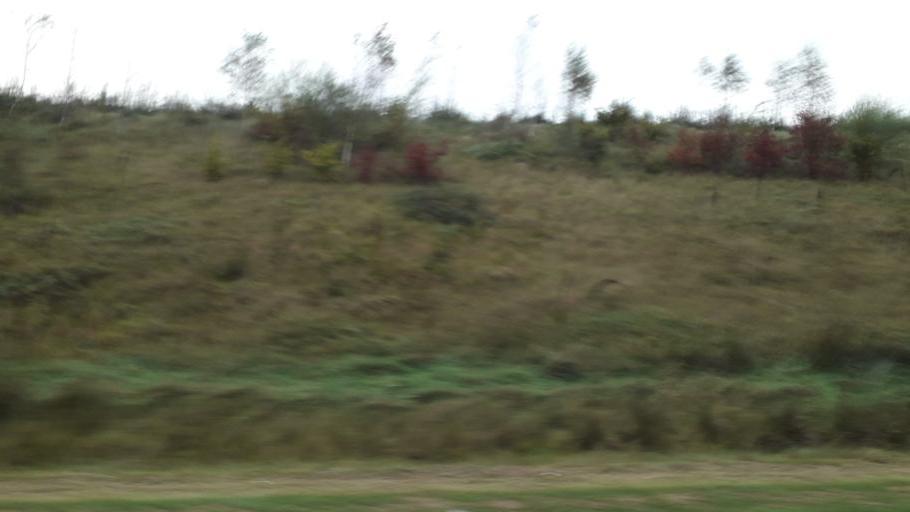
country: IE
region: Leinster
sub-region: An Longfort
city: Longford
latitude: 53.7290
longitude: -7.8253
